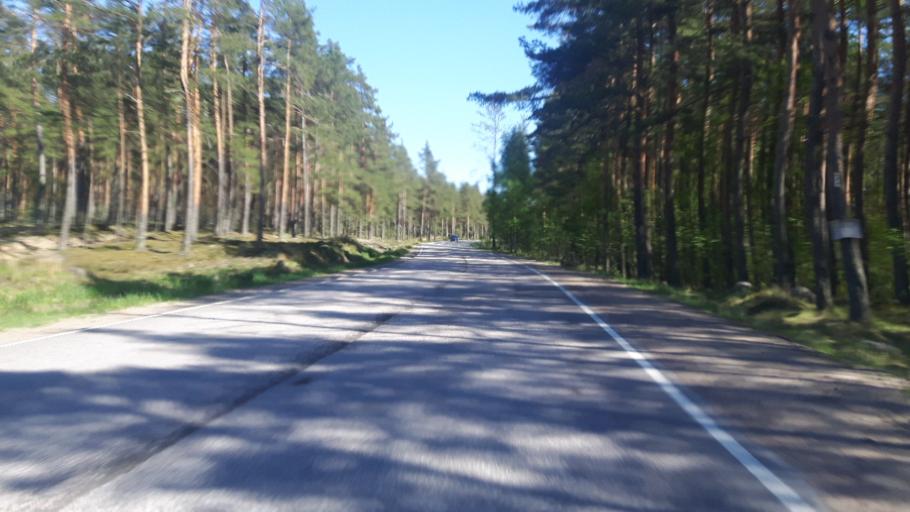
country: RU
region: Leningrad
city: Glebychevo
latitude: 60.2763
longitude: 28.9250
